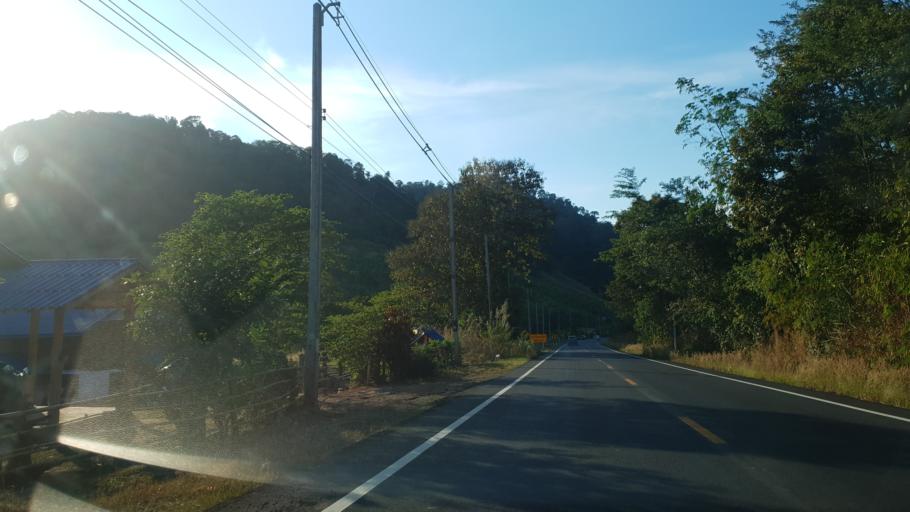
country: TH
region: Loei
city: Dan Sai
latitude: 17.2247
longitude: 101.0641
